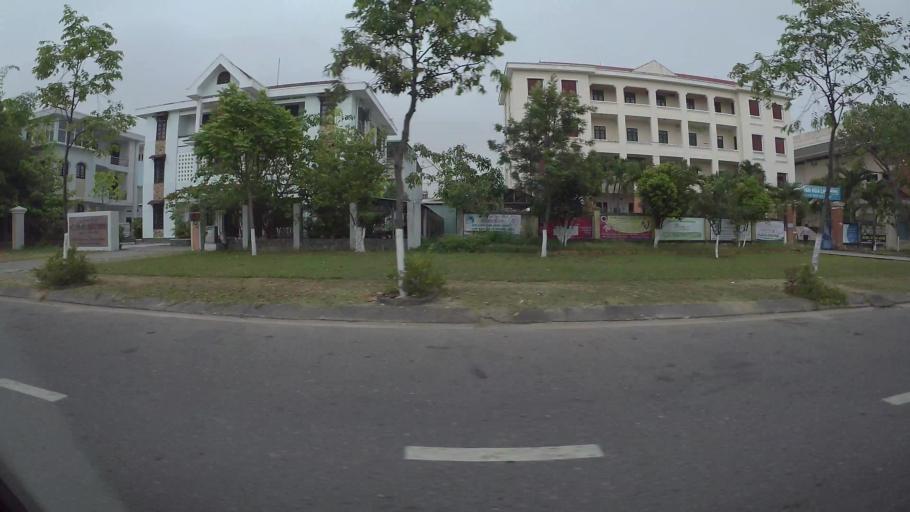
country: VN
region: Da Nang
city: Cam Le
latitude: 16.0273
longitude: 108.2198
